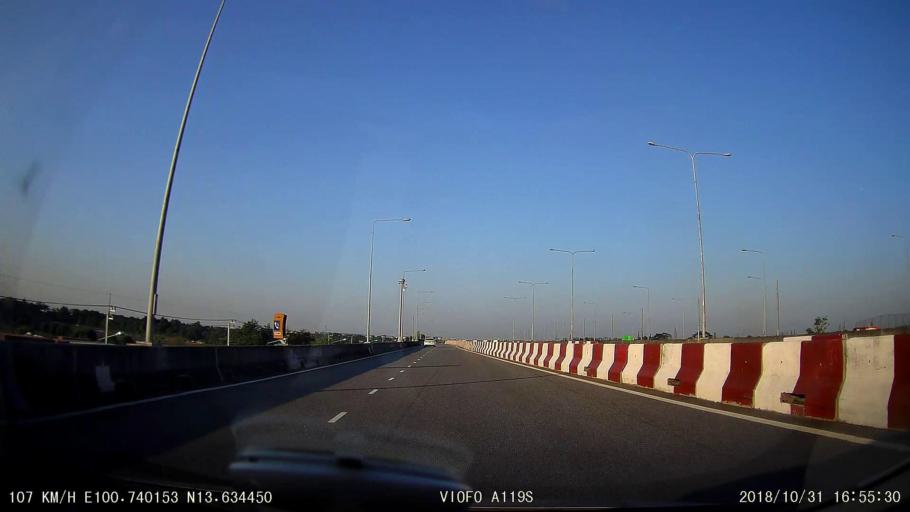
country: TH
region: Samut Prakan
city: Bang Bo District
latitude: 13.6348
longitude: 100.7403
